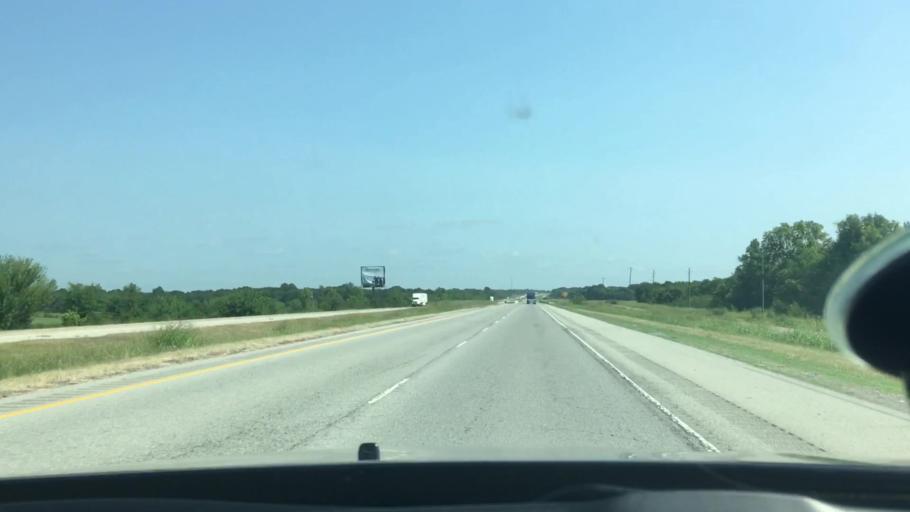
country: US
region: Oklahoma
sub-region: Atoka County
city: Atoka
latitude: 34.2446
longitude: -96.2177
